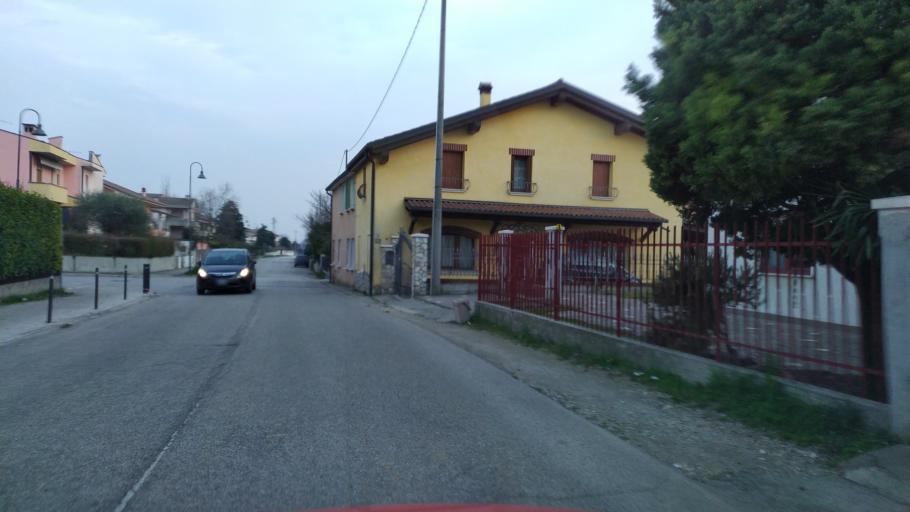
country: IT
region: Veneto
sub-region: Provincia di Vicenza
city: Dueville
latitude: 45.6258
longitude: 11.5745
